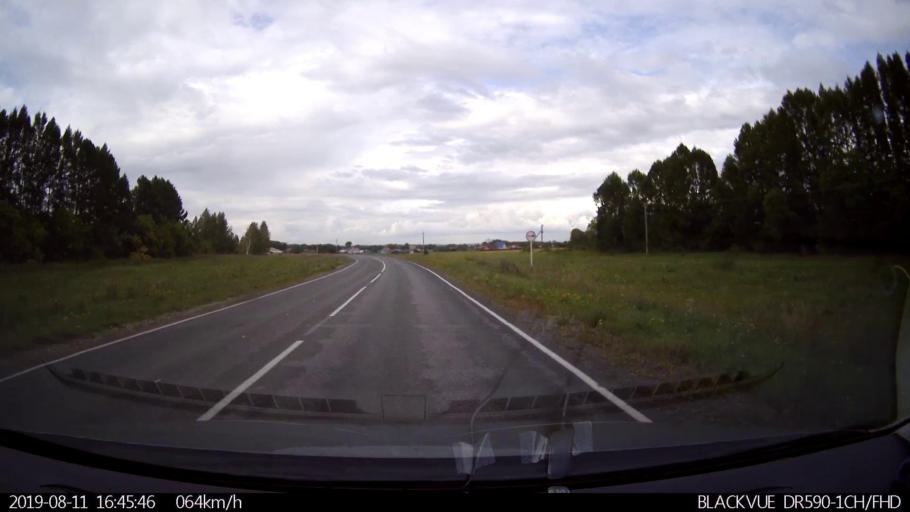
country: RU
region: Ulyanovsk
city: Mayna
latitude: 54.1931
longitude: 47.6879
